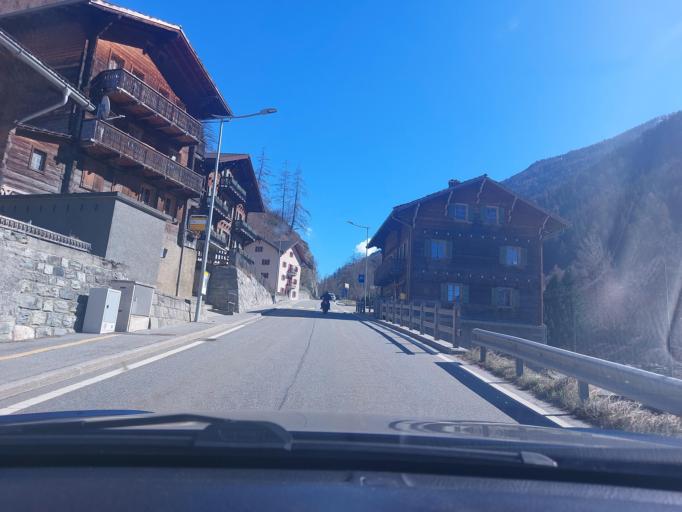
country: CH
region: Valais
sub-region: Herens District
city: Evolene
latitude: 46.1505
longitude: 7.4543
